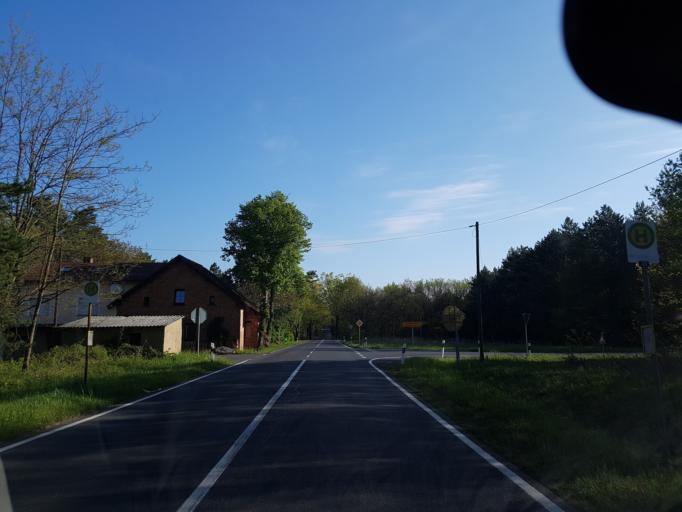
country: DE
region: Brandenburg
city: Grossraschen
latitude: 51.6113
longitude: 14.0209
